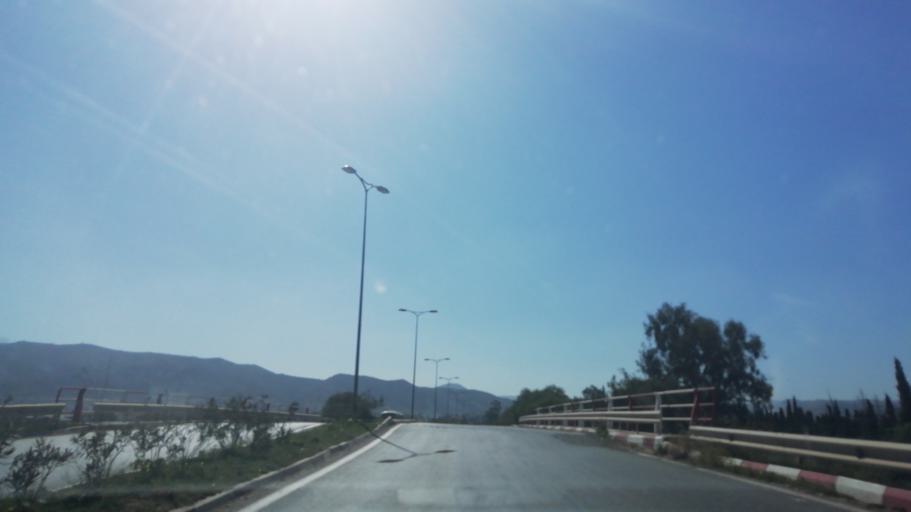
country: DZ
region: Mascara
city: Sig
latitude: 35.5397
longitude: -0.2040
